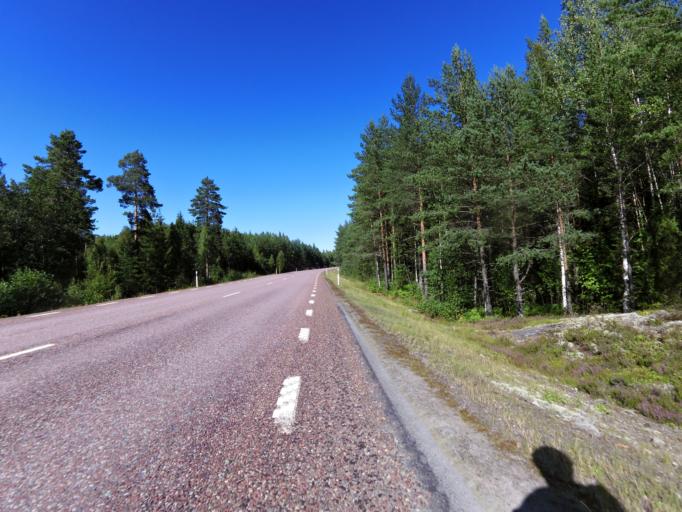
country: SE
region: Gaevleborg
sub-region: Hofors Kommun
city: Hofors
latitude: 60.5529
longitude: 16.4770
